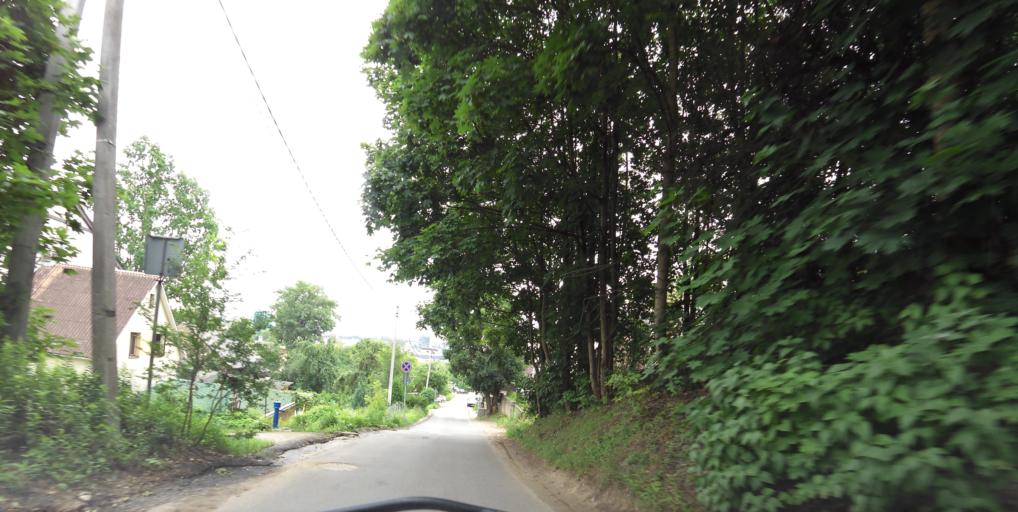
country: LT
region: Vilnius County
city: Seskine
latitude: 54.7046
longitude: 25.2551
